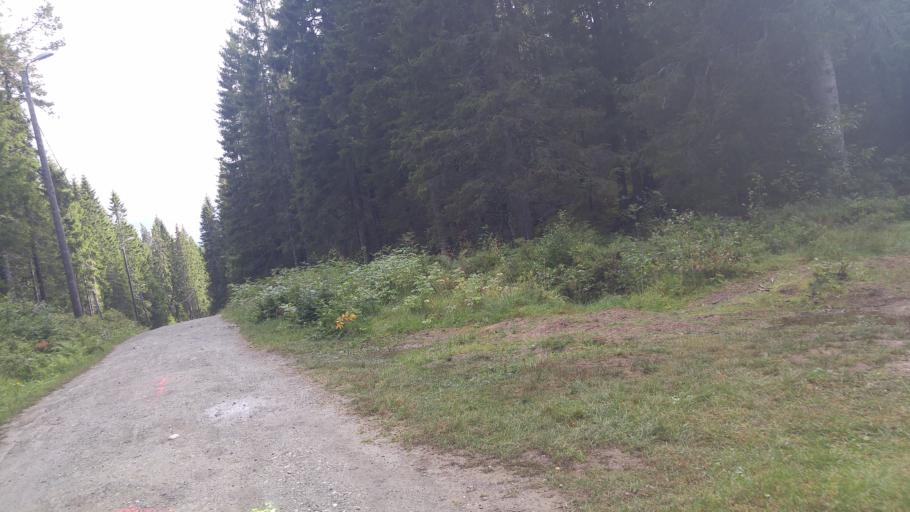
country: NO
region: Sor-Trondelag
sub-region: Trondheim
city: Trondheim
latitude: 63.4123
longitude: 10.3308
